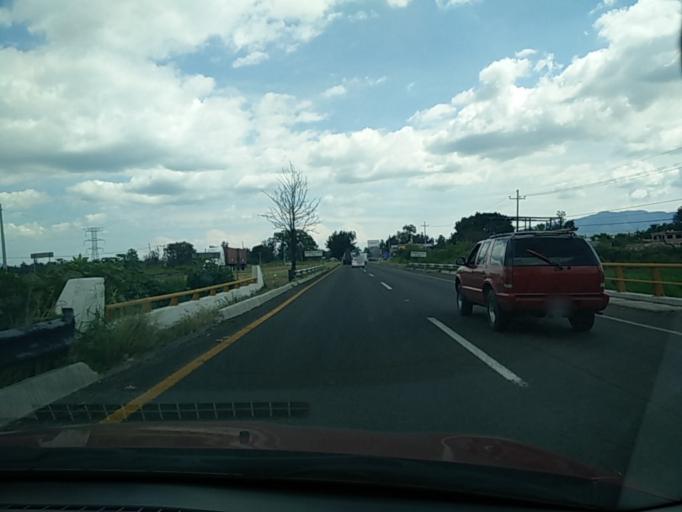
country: MX
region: Jalisco
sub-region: Tlajomulco de Zuniga
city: Rancho Alegre [Fraccionamiento]
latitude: 20.4608
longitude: -103.2545
